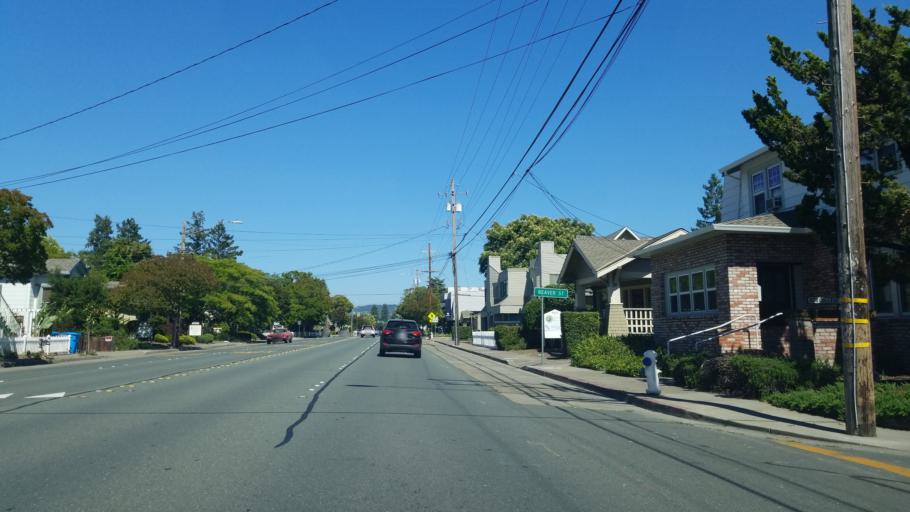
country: US
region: California
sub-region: Sonoma County
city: Santa Rosa
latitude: 38.4455
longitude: -122.7135
